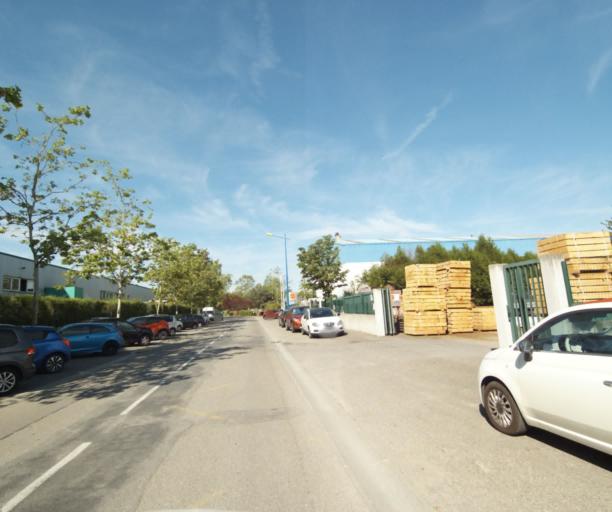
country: FR
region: Rhone-Alpes
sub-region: Departement de la Haute-Savoie
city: Marin
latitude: 46.3955
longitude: 6.5078
